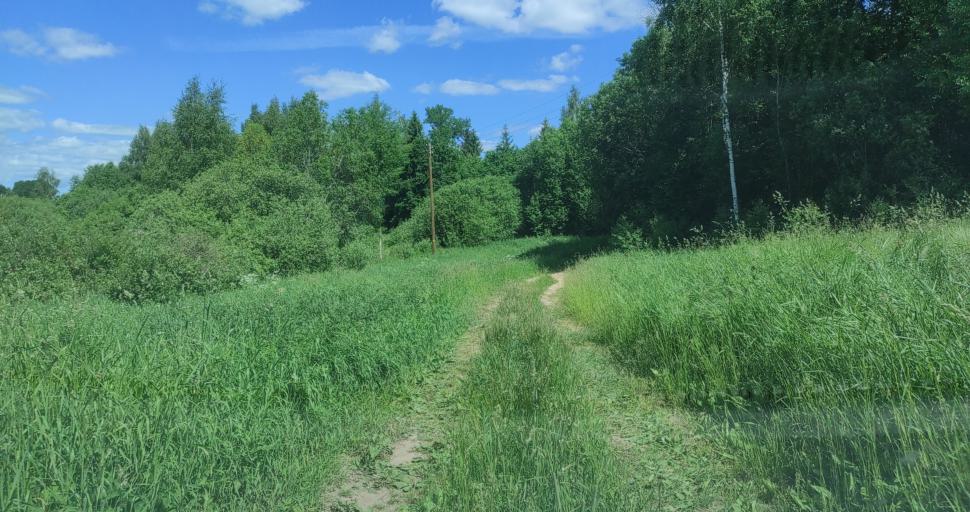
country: LV
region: Aizpute
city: Aizpute
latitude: 56.8612
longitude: 21.7291
